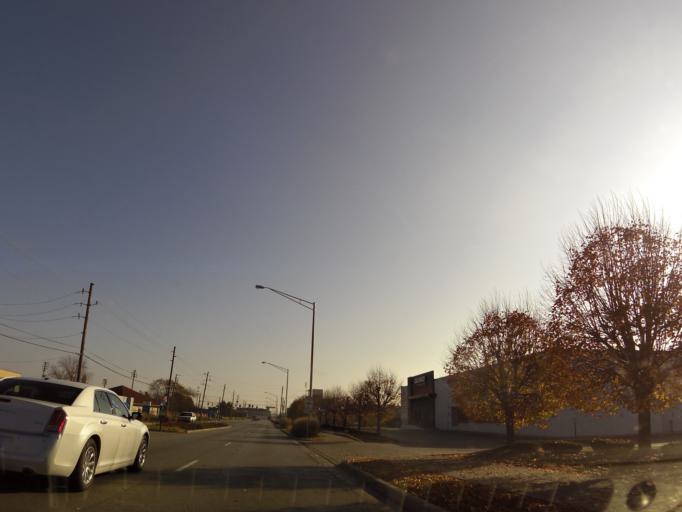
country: US
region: Indiana
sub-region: Marion County
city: Indianapolis
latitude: 39.7892
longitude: -86.1934
